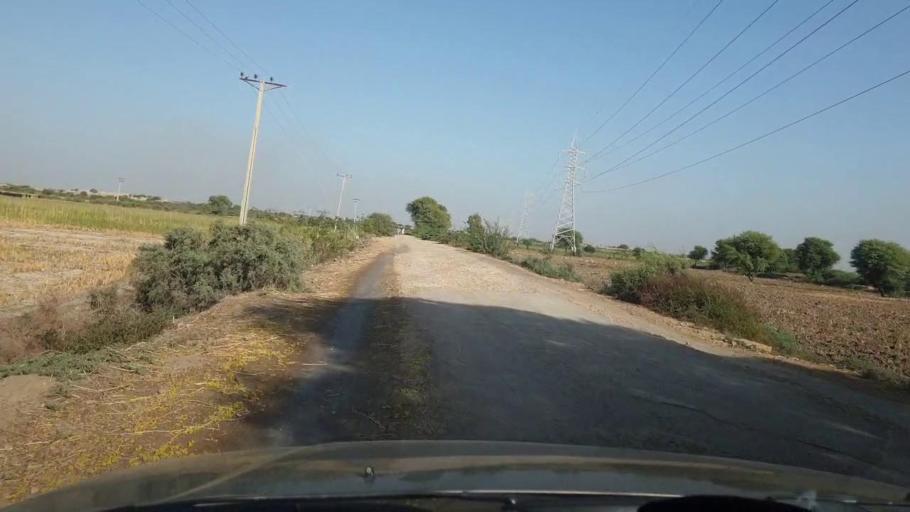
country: PK
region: Sindh
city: Bulri
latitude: 25.1088
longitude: 68.2563
